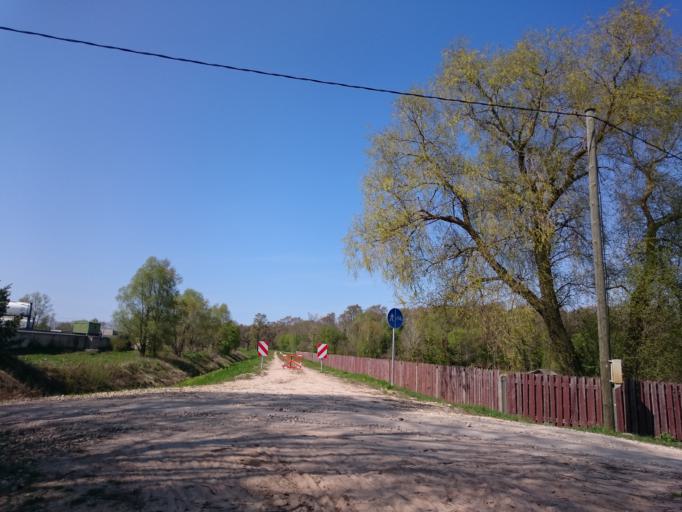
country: LV
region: Adazi
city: Adazi
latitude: 57.0988
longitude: 24.3288
